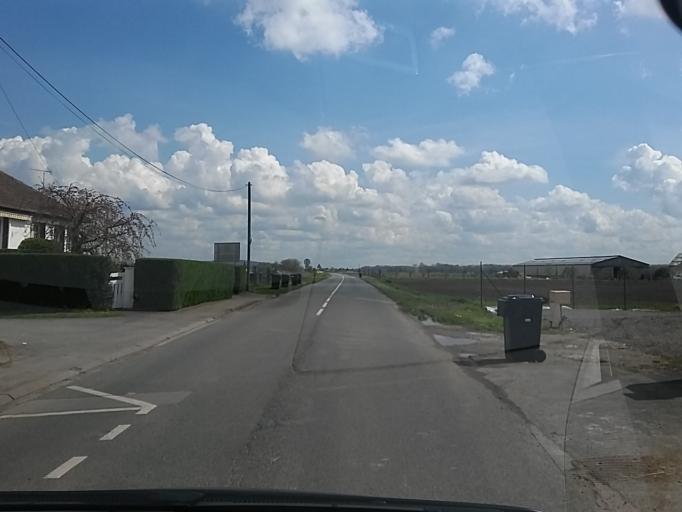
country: FR
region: Picardie
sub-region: Departement de l'Oise
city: Grandfresnoy
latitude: 49.3453
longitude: 2.6444
